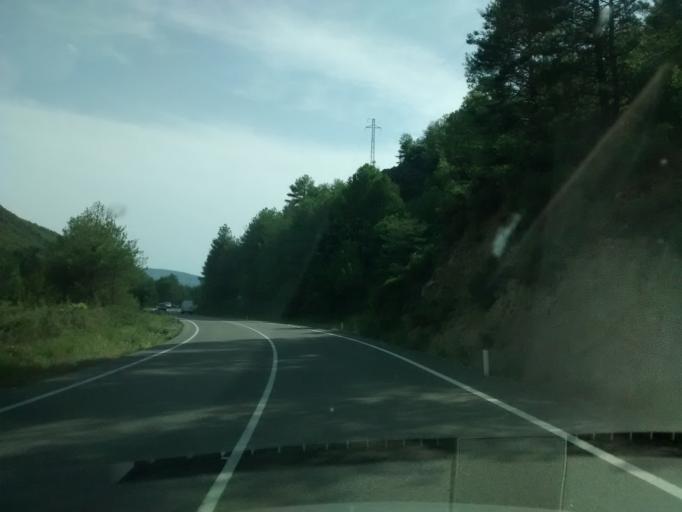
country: ES
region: Aragon
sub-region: Provincia de Huesca
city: Labuerda
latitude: 42.4763
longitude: 0.1485
